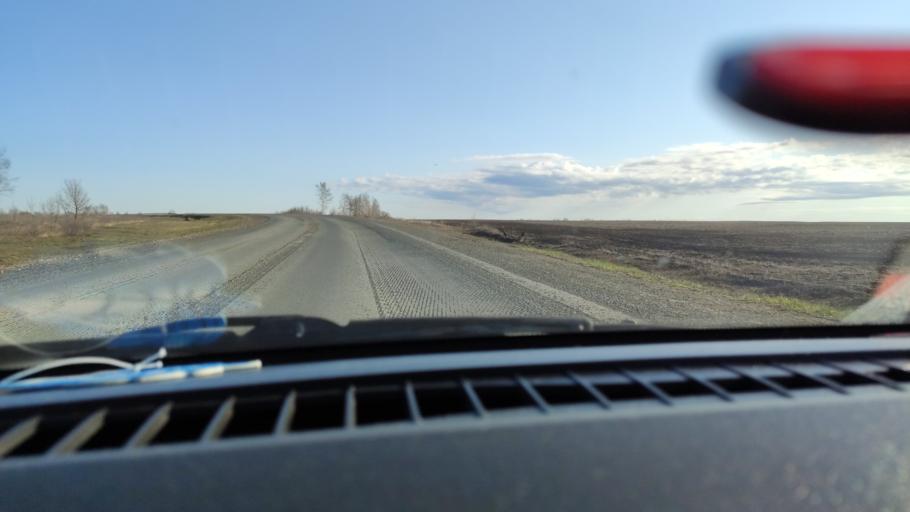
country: RU
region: Saratov
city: Dukhovnitskoye
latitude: 52.7113
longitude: 48.2660
